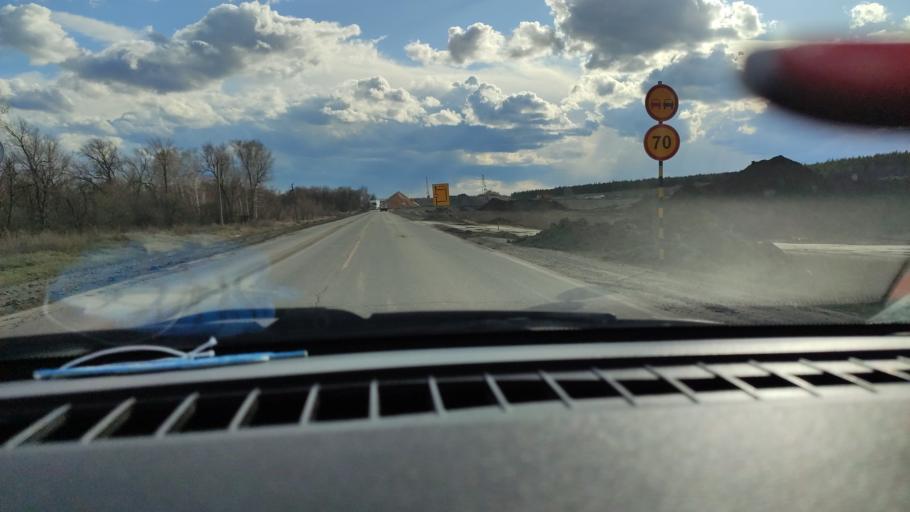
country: RU
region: Saratov
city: Sinodskoye
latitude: 52.0143
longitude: 46.6945
